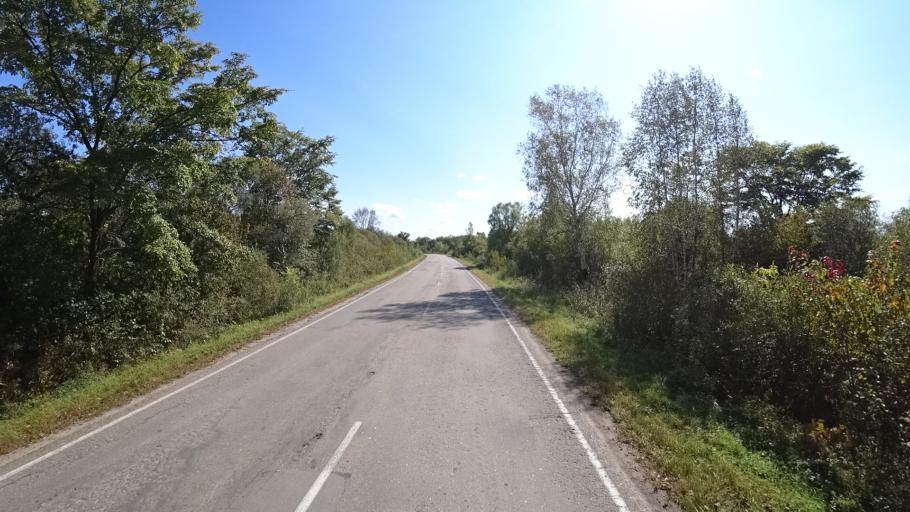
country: RU
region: Amur
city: Arkhara
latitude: 49.4027
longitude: 130.1290
